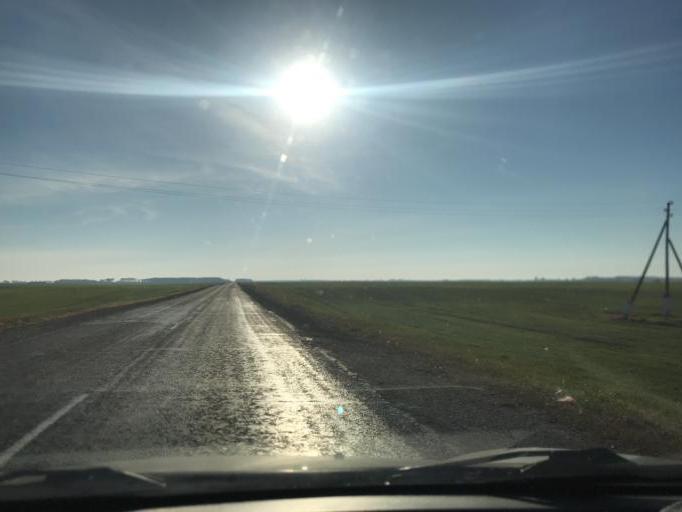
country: BY
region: Gomel
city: Khoyniki
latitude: 51.8341
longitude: 30.0498
